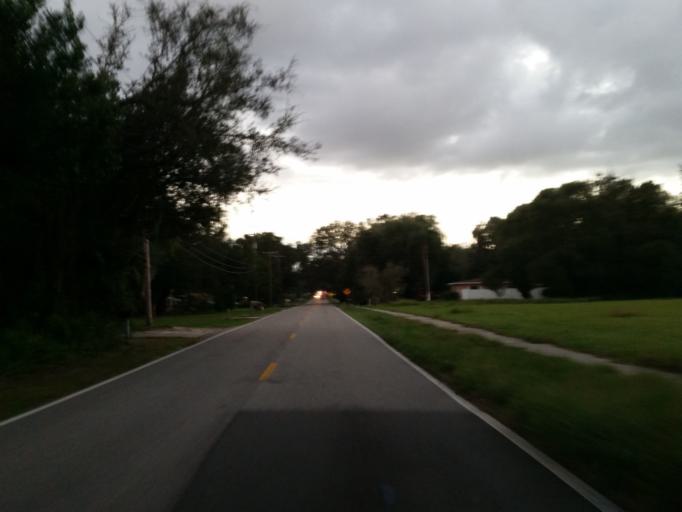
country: US
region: Florida
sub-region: Hillsborough County
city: Brandon
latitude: 27.9177
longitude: -82.2693
